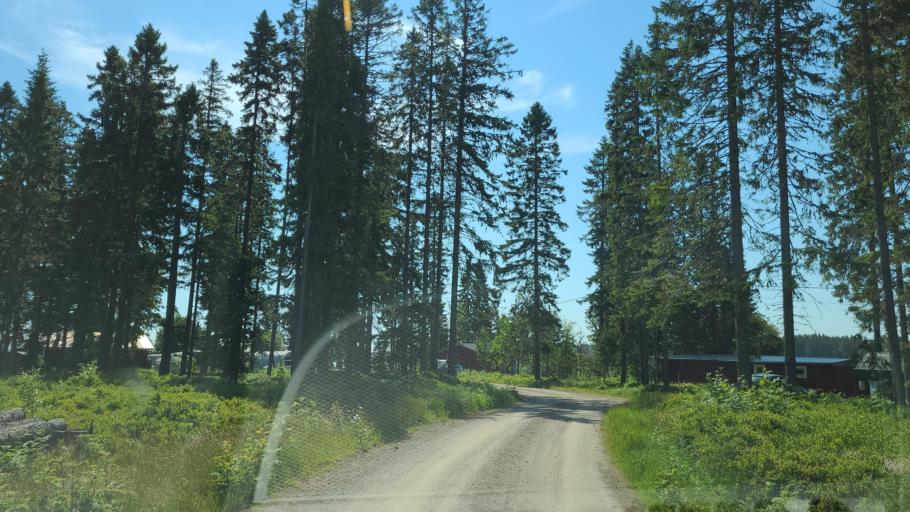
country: SE
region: Vaesterbotten
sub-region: Robertsfors Kommun
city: Robertsfors
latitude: 64.1390
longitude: 20.9633
